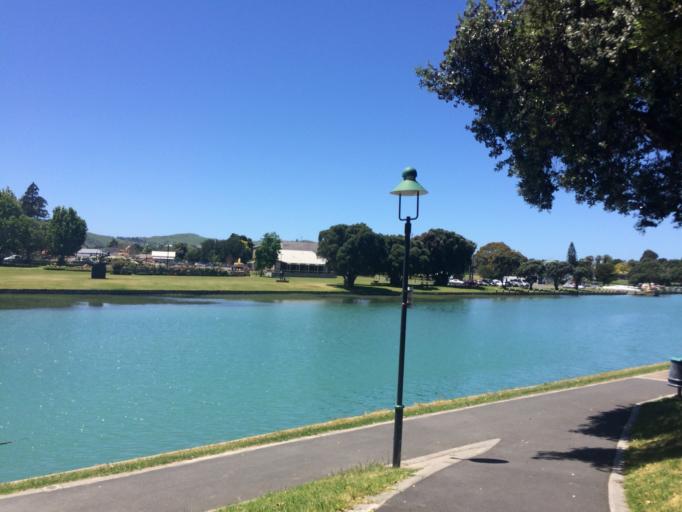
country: NZ
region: Gisborne
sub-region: Gisborne District
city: Gisborne
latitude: -38.6655
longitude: 178.0275
